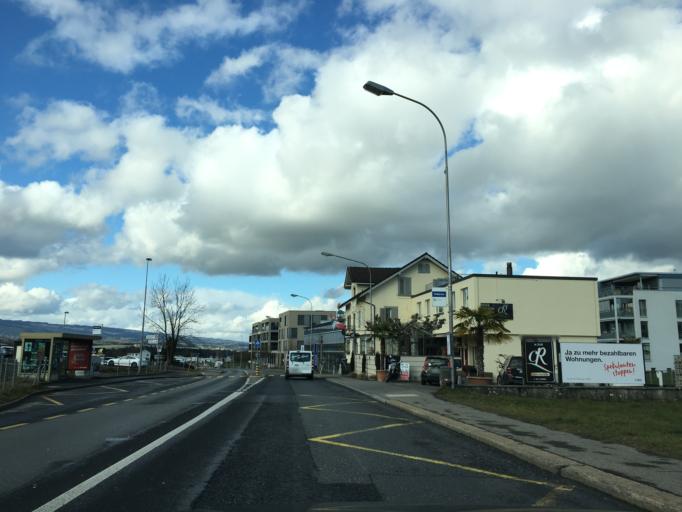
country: CH
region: Zug
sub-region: Zug
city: Cham
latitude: 47.1933
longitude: 8.4440
